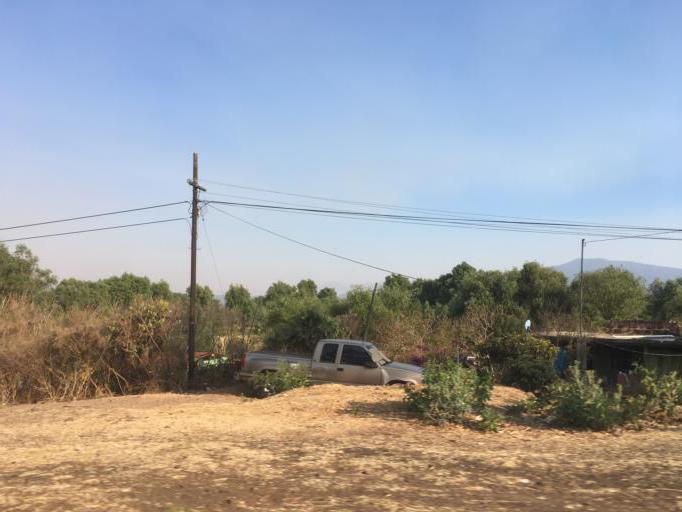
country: MX
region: Michoacan
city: Santa Fe de la Laguna
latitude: 19.6713
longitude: -101.5610
